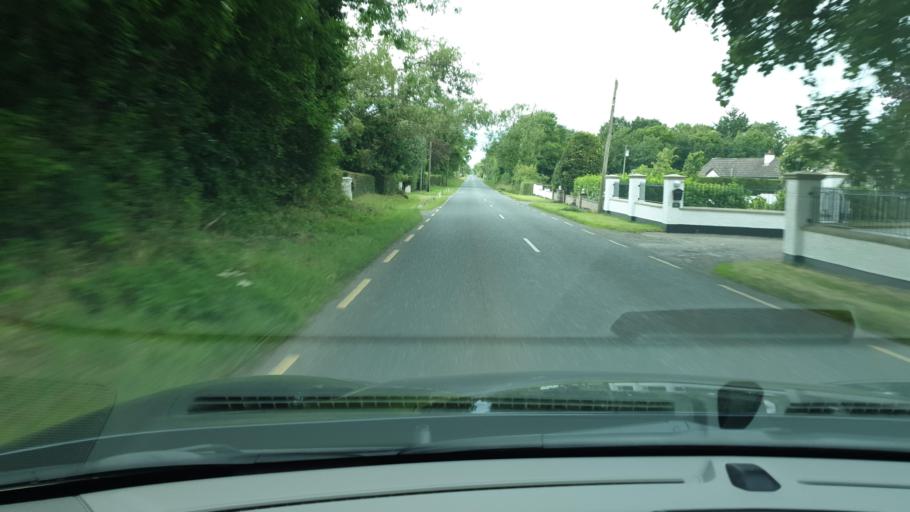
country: IE
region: Leinster
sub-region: An Mhi
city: Ratoath
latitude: 53.5318
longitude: -6.4901
